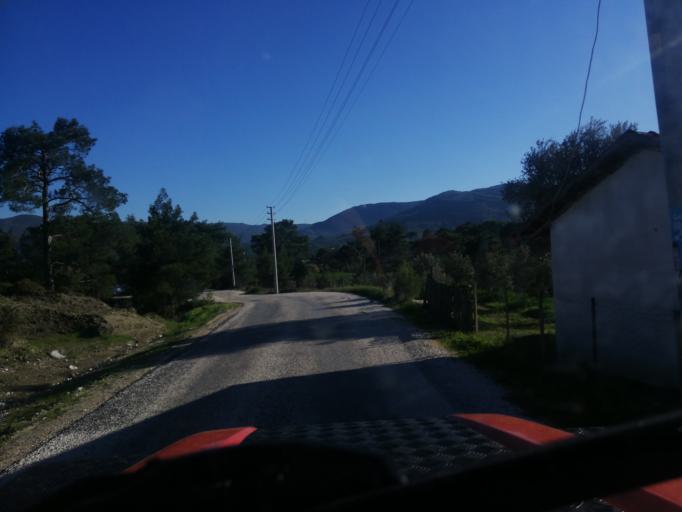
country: TR
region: Antalya
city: Kas
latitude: 36.2947
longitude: 29.7055
